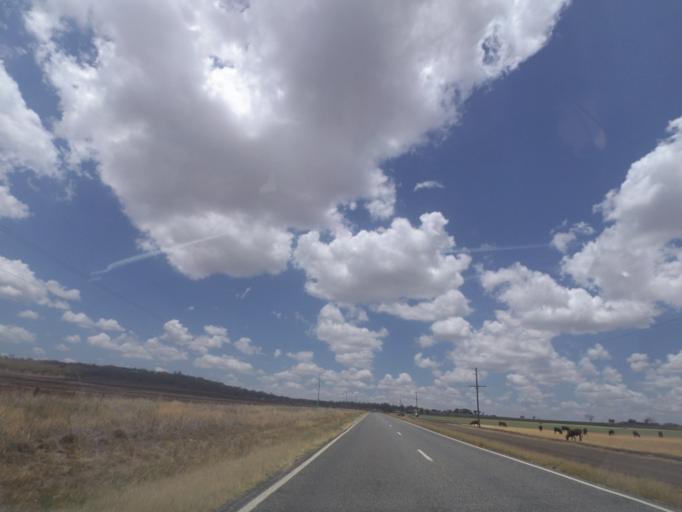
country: AU
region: Queensland
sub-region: Toowoomba
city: Top Camp
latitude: -27.8728
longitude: 151.9630
